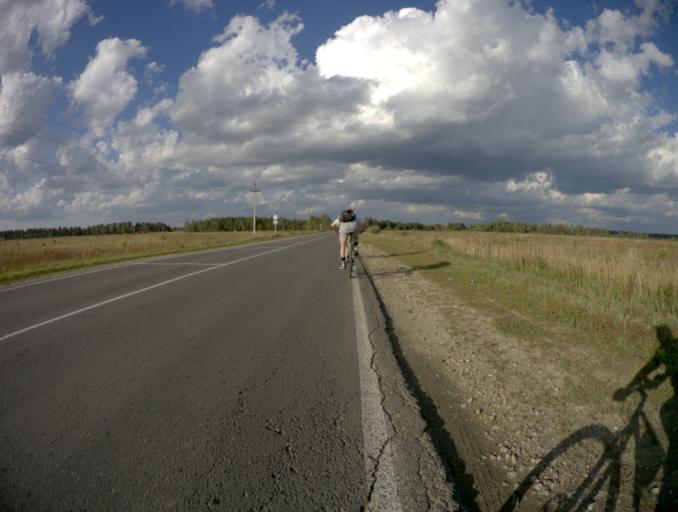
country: RU
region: Vladimir
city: Raduzhnyy
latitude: 56.0249
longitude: 40.3367
